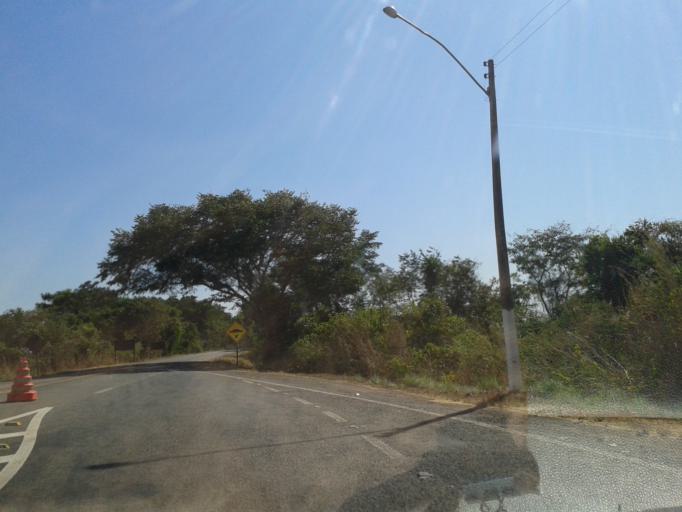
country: BR
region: Goias
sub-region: Crixas
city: Crixas
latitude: -13.9653
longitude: -50.3208
